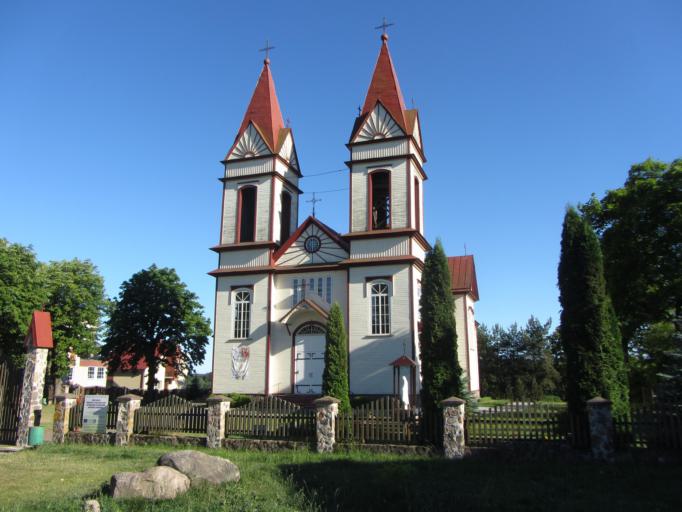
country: LT
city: Aukstadvaris
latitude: 54.5788
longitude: 24.5341
